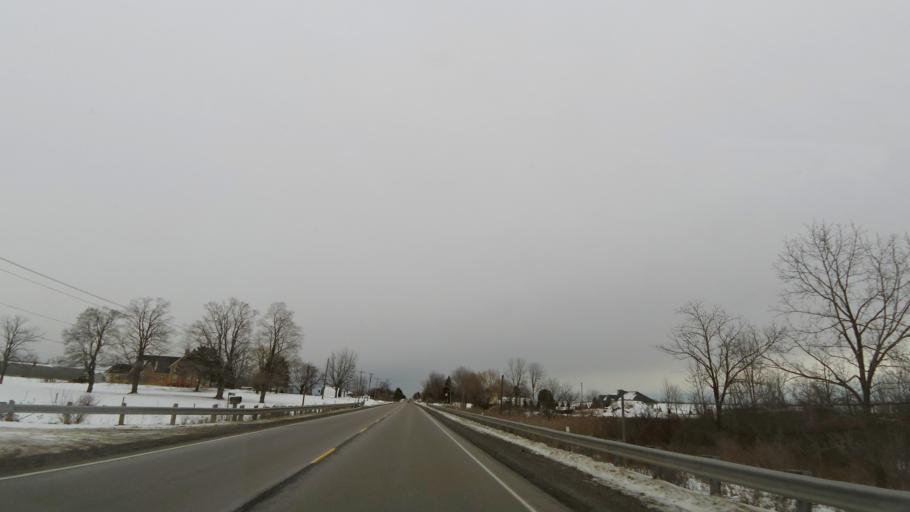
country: CA
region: Ontario
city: Ancaster
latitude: 43.2971
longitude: -79.9733
